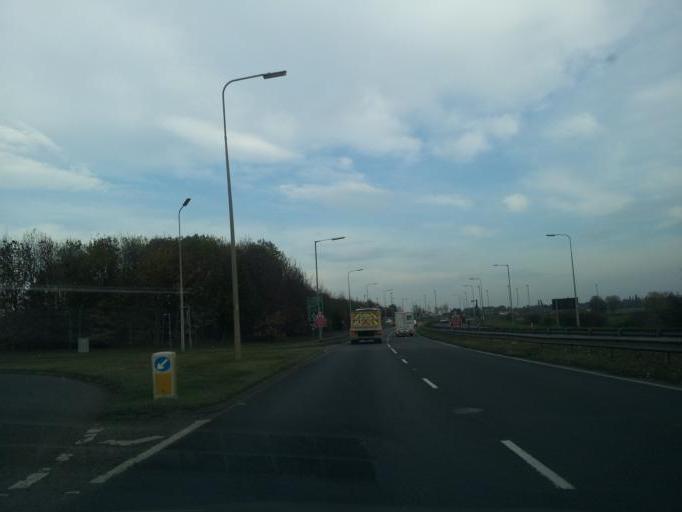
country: GB
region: England
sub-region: Cambridgeshire
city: Duxford
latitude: 52.1000
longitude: 0.1411
